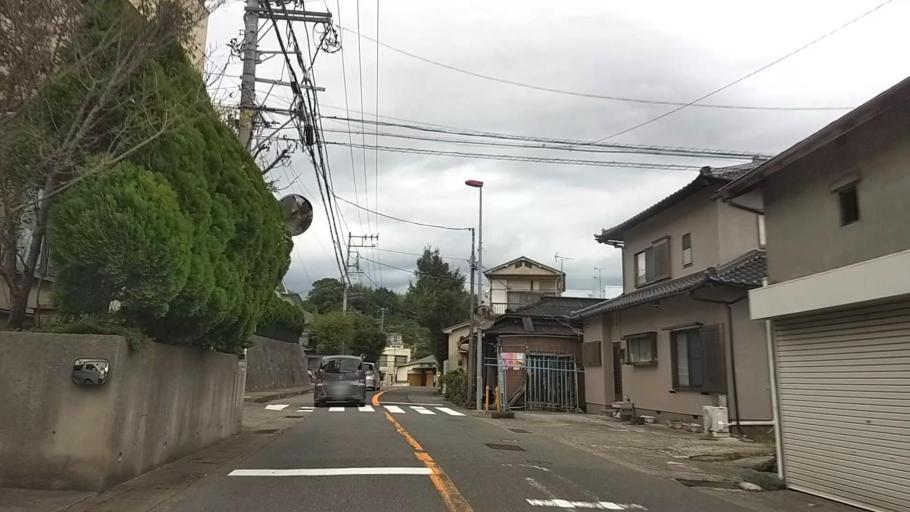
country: JP
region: Kanagawa
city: Odawara
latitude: 35.1912
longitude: 139.1332
